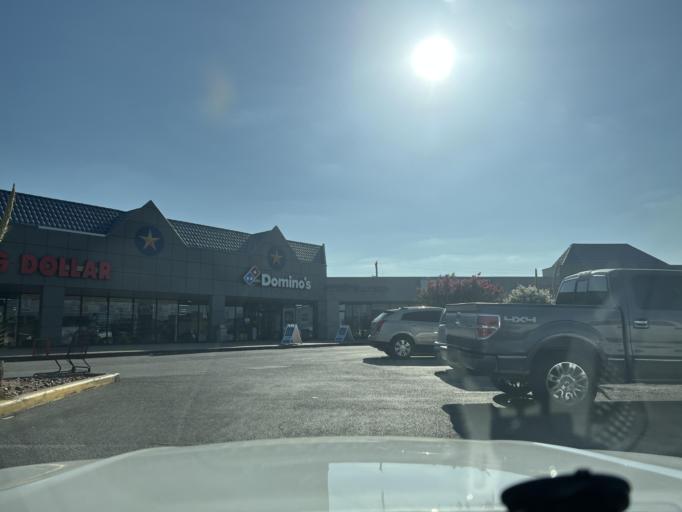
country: US
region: Texas
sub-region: Washington County
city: Brenham
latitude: 30.1406
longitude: -96.3974
